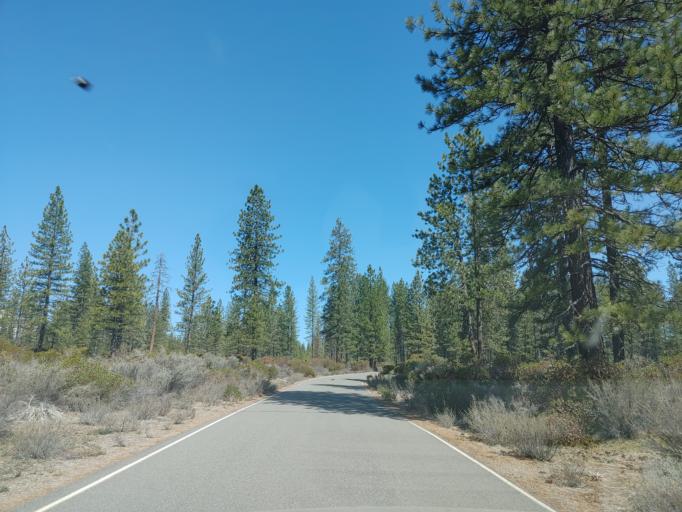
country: US
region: California
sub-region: Siskiyou County
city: McCloud
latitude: 41.2462
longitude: -122.0282
